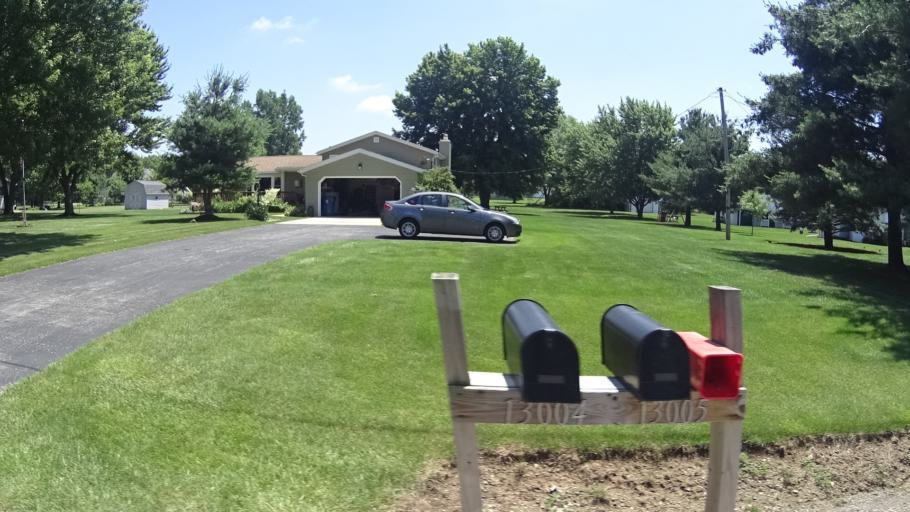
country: US
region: Ohio
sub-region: Lorain County
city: Vermilion
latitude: 41.3558
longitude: -82.3966
